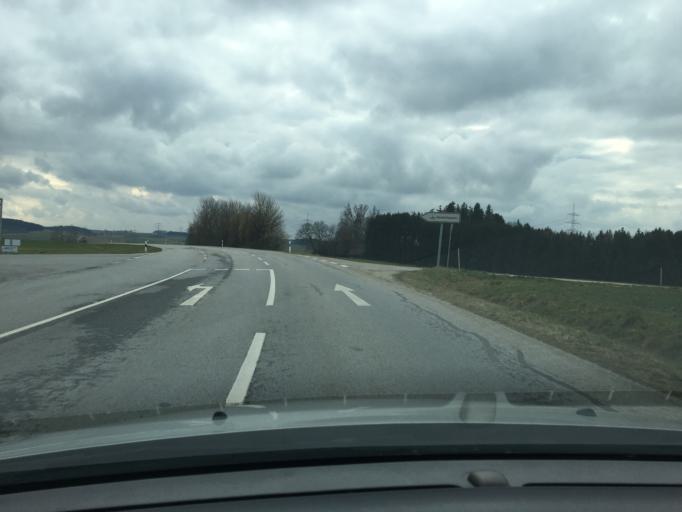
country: DE
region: Bavaria
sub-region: Lower Bavaria
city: Geisenhausen
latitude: 48.4830
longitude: 12.2415
